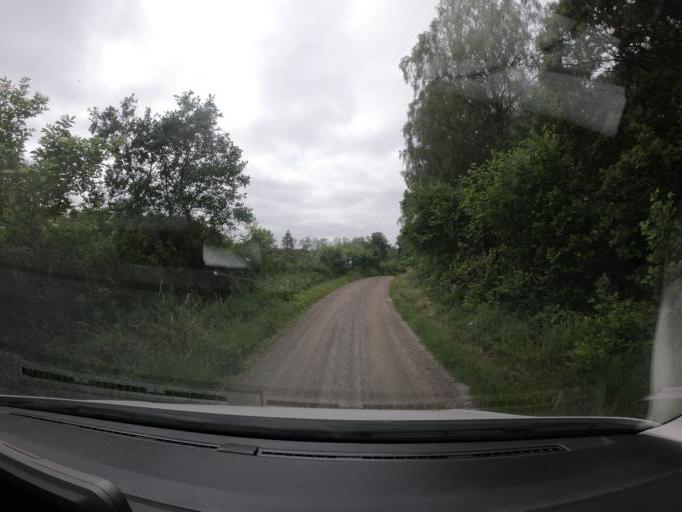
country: SE
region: Skane
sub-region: Hassleholms Kommun
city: Sosdala
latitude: 56.0215
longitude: 13.6135
